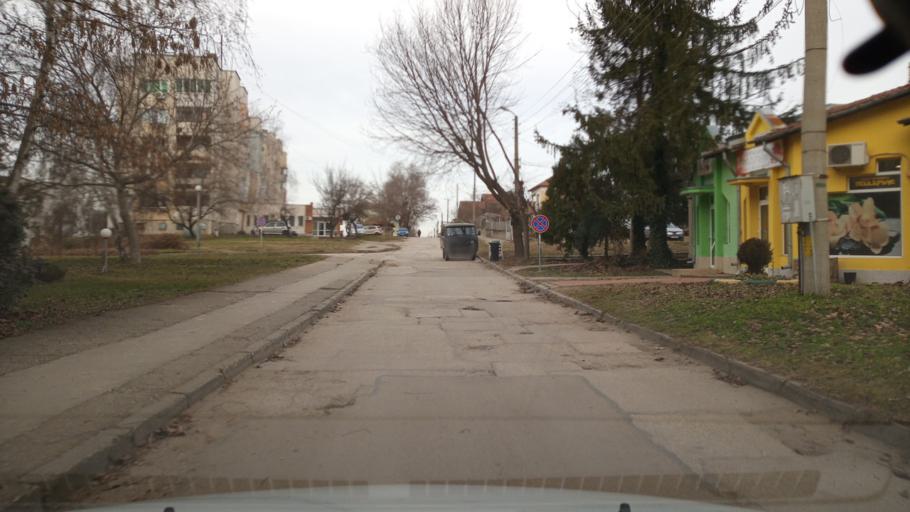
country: BG
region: Pleven
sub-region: Obshtina Belene
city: Belene
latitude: 43.6453
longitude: 25.1244
